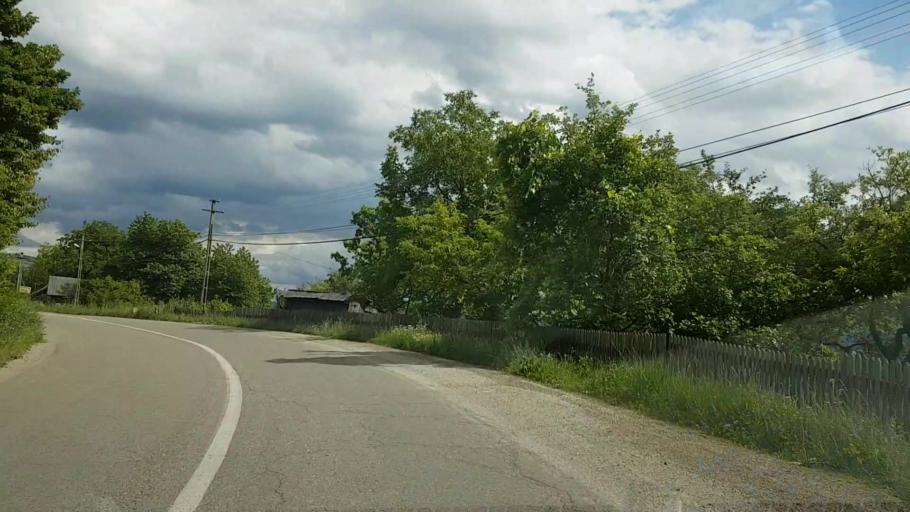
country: RO
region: Neamt
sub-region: Comuna Hangu
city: Hangu
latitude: 47.0263
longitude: 26.0671
